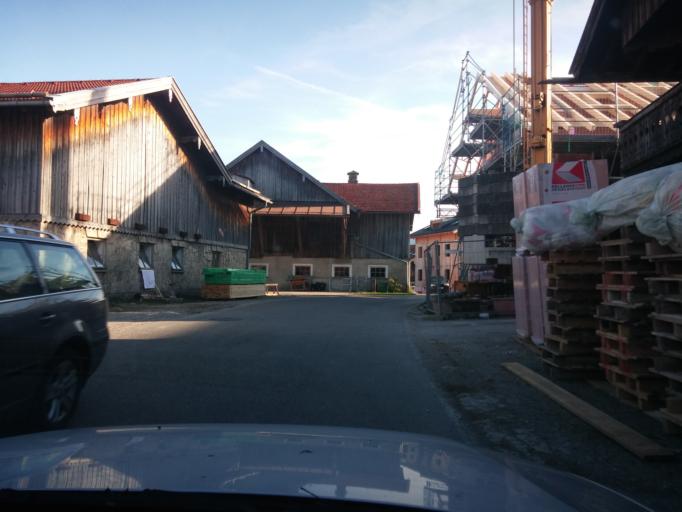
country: DE
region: Bavaria
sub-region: Upper Bavaria
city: Gaissach
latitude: 47.7820
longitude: 11.5848
